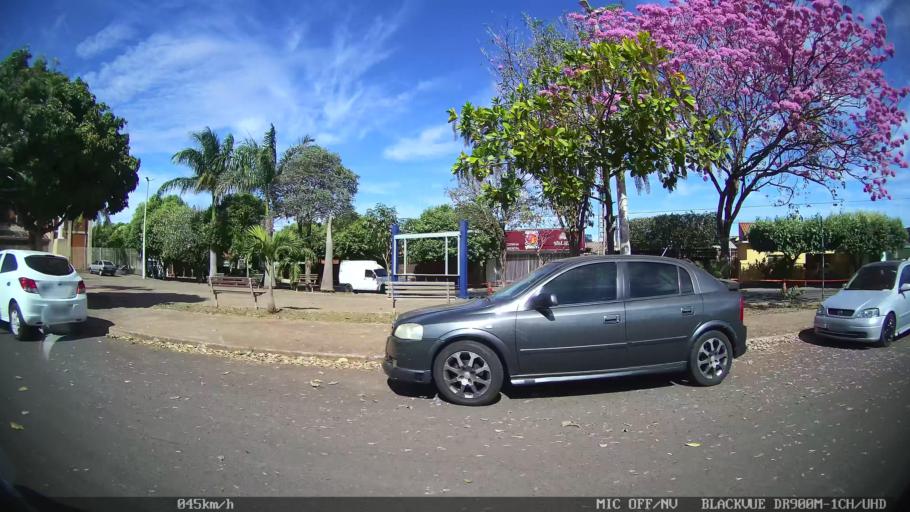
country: BR
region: Sao Paulo
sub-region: Bady Bassitt
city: Bady Bassitt
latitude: -20.8216
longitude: -49.4922
